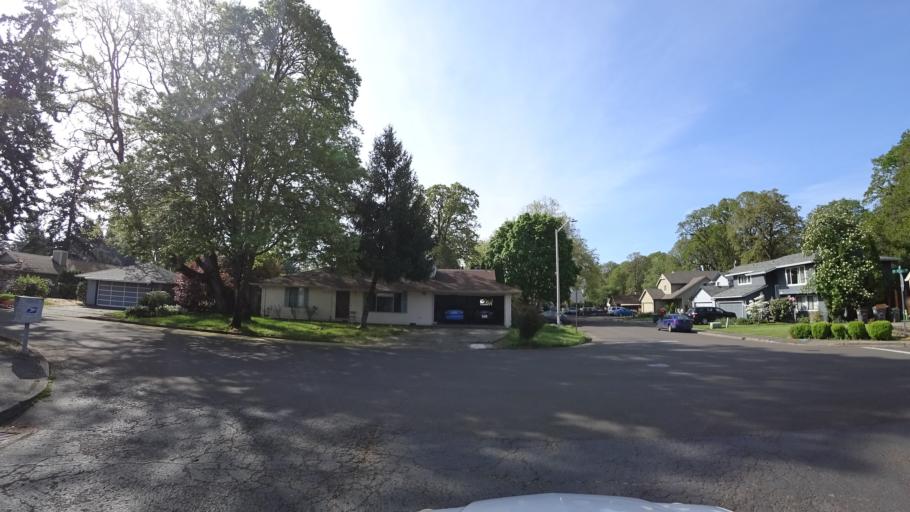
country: US
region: Oregon
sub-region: Washington County
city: Hillsboro
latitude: 45.5259
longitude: -122.9579
